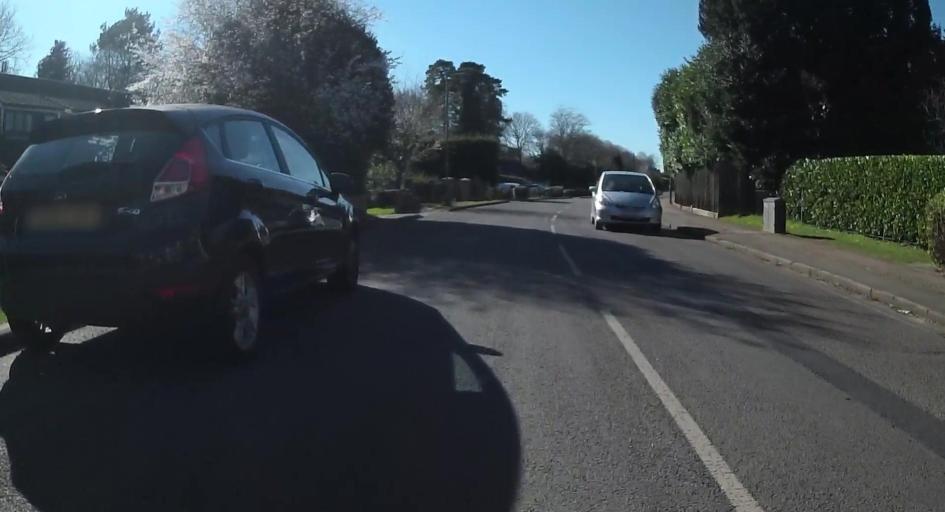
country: GB
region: England
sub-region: Surrey
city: Walton-on-Thames
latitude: 51.3708
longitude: -0.4277
